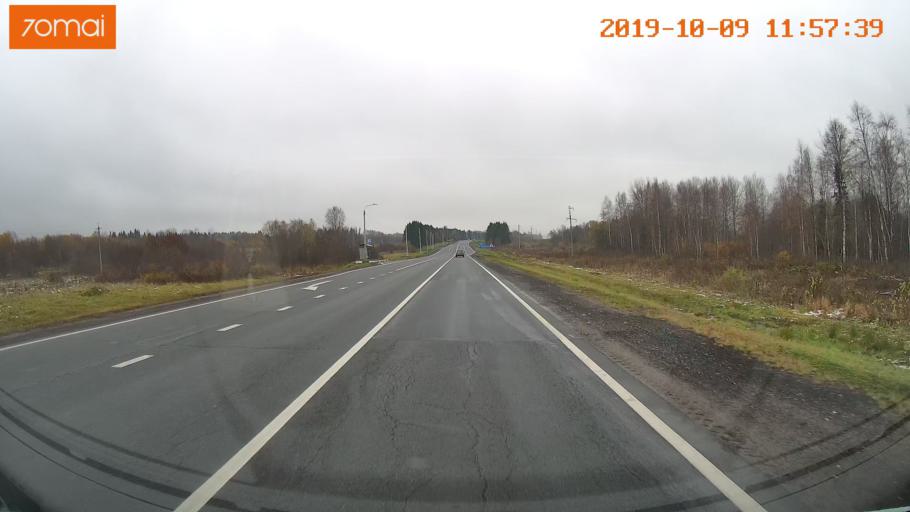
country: RU
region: Vologda
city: Gryazovets
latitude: 58.7294
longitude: 40.2938
